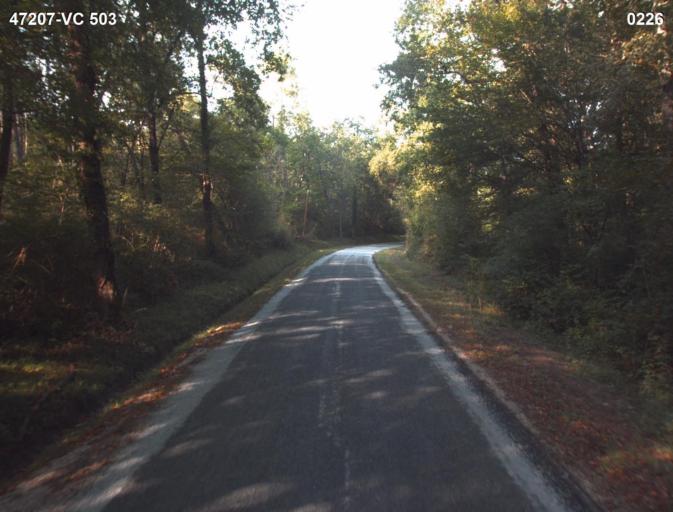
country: FR
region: Aquitaine
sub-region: Departement du Lot-et-Garonne
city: Barbaste
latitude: 44.2043
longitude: 0.2339
